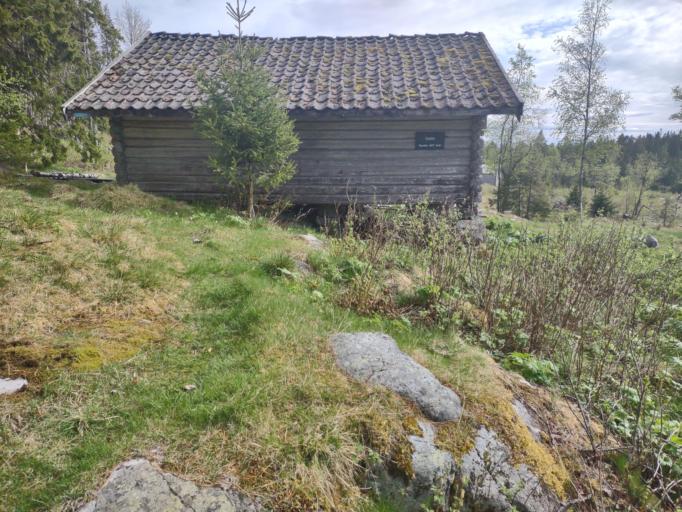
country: NO
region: Oppland
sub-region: Gran
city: Jaren
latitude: 60.4754
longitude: 10.5599
